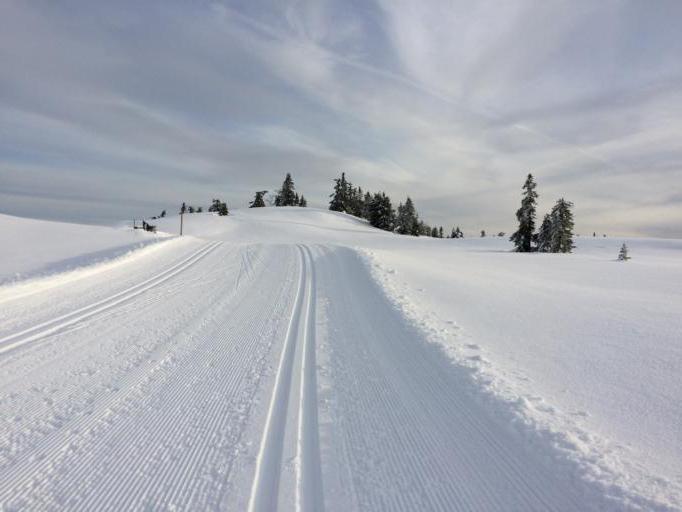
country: NO
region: Oppland
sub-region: Gausdal
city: Segalstad bru
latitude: 61.3251
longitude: 10.0394
